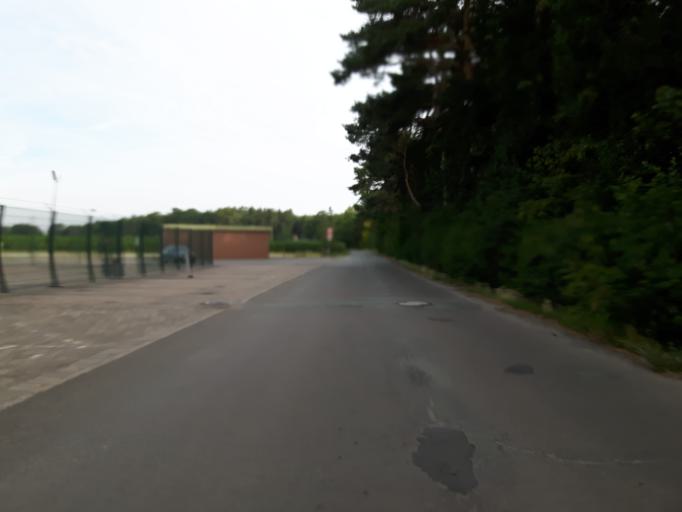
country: DE
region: Lower Saxony
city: Delmenhorst
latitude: 53.0801
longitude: 8.6444
